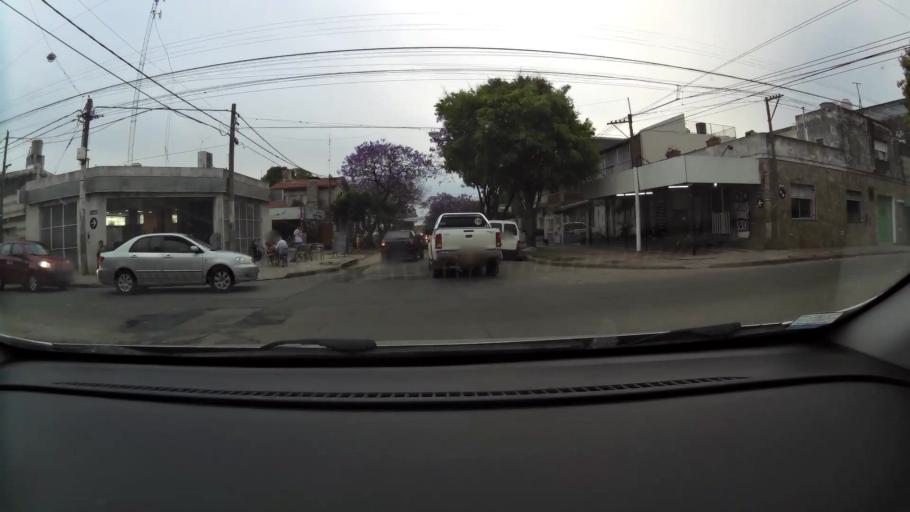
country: AR
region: Santa Fe
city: Granadero Baigorria
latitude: -32.8938
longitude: -60.7047
